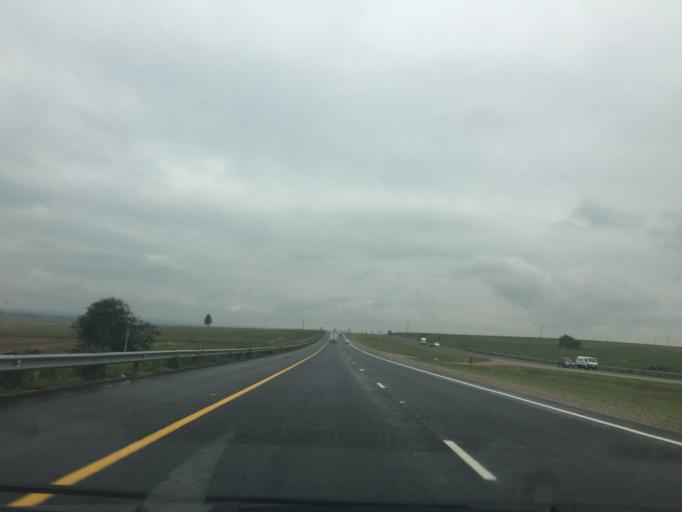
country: ZA
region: Gauteng
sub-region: City of Johannesburg Metropolitan Municipality
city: Diepsloot
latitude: -25.9369
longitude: 27.9776
